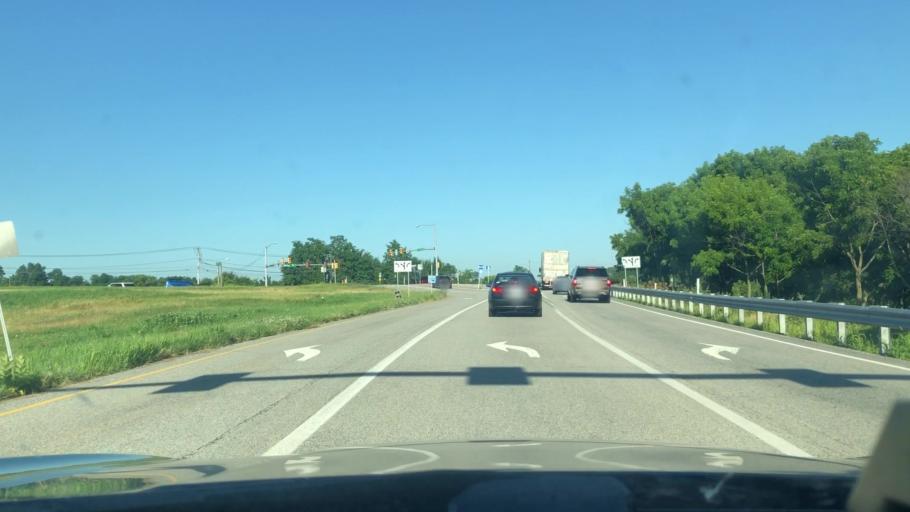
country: US
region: Pennsylvania
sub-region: Cumberland County
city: Shiremanstown
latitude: 40.2099
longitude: -76.9572
